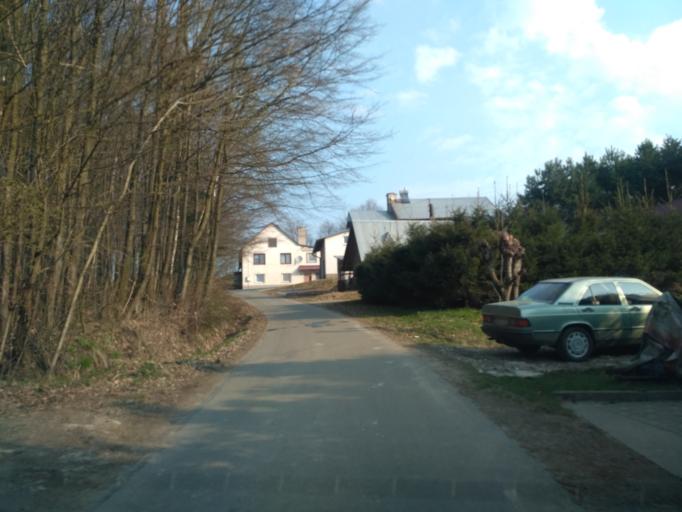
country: PL
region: Subcarpathian Voivodeship
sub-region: Powiat strzyzowski
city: Wisniowa
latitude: 49.8845
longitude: 21.6341
